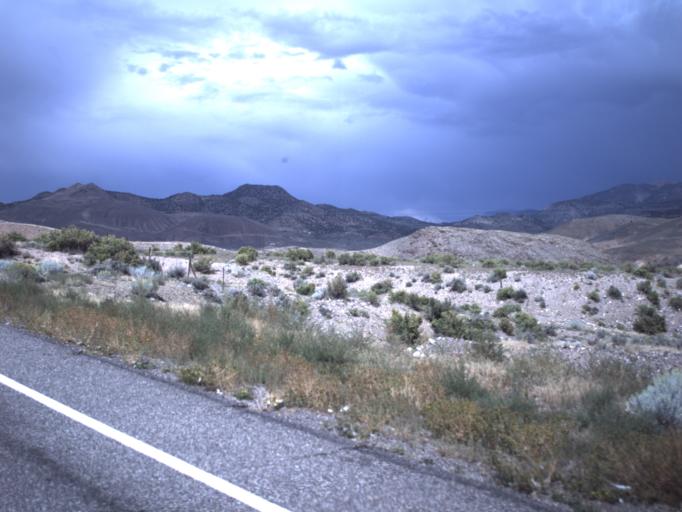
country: US
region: Utah
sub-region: Sevier County
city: Monroe
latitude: 38.4556
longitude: -112.2308
